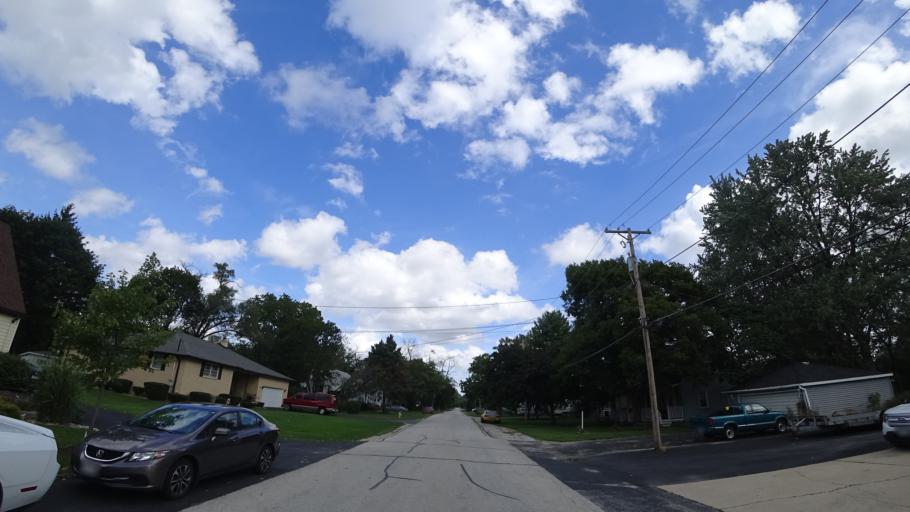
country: US
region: Illinois
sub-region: Cook County
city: Tinley Park
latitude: 41.5702
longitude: -87.7769
